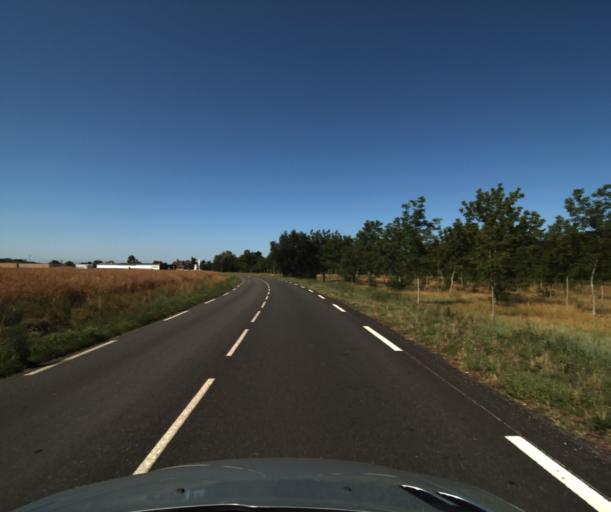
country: FR
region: Midi-Pyrenees
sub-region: Departement de la Haute-Garonne
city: Roquettes
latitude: 43.5046
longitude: 1.3742
